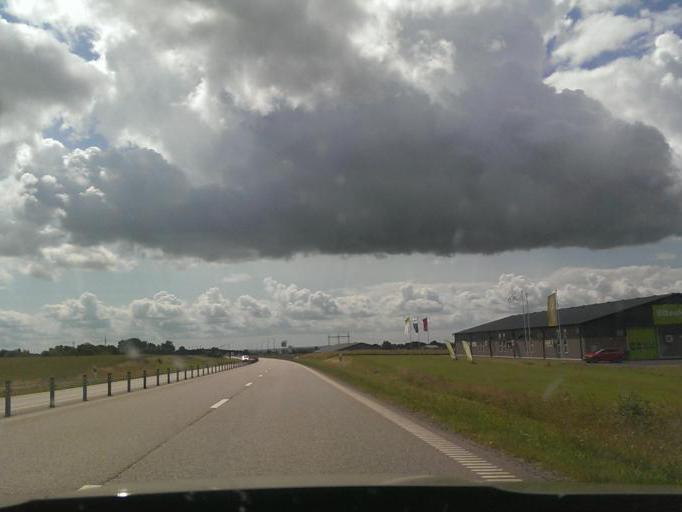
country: SE
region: Skane
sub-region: Eslovs Kommun
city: Eslov
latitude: 55.8314
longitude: 13.3318
